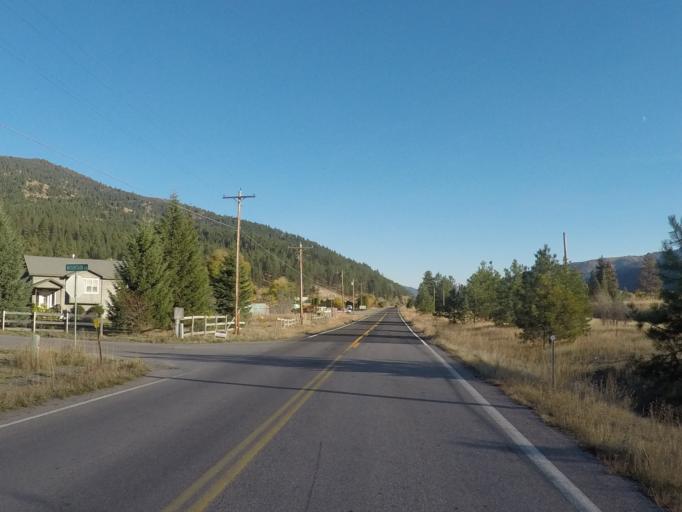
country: US
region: Montana
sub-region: Missoula County
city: Bonner-West Riverside
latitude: 46.8364
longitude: -113.8271
